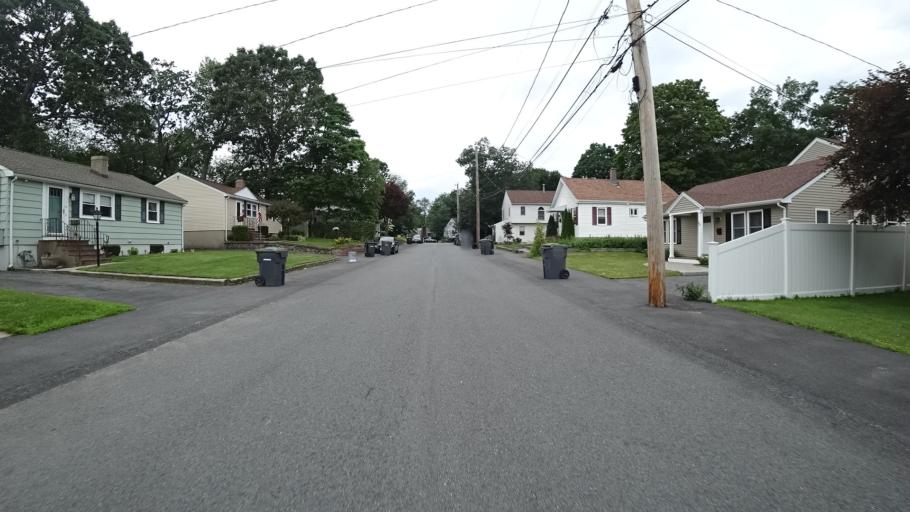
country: US
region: Massachusetts
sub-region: Norfolk County
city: Dedham
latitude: 42.2339
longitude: -71.1495
